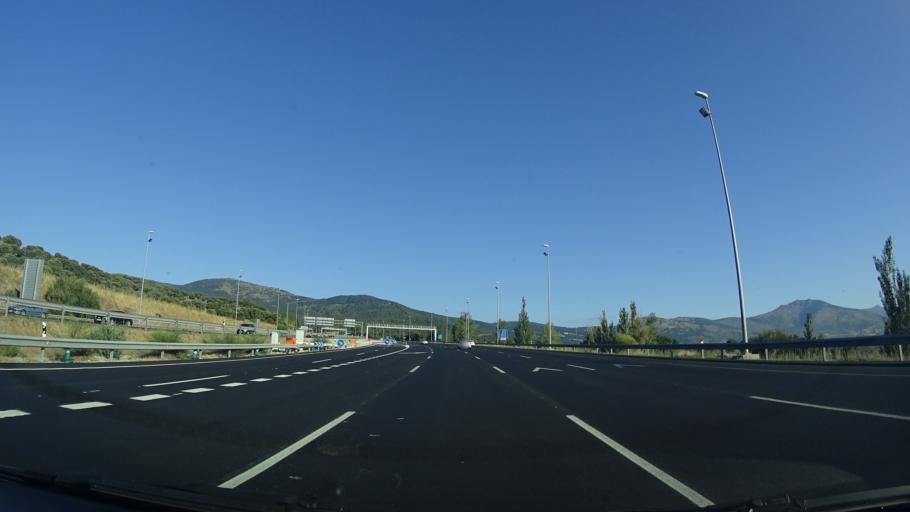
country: ES
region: Madrid
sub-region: Provincia de Madrid
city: Guadarrama
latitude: 40.6667
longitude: -4.1019
